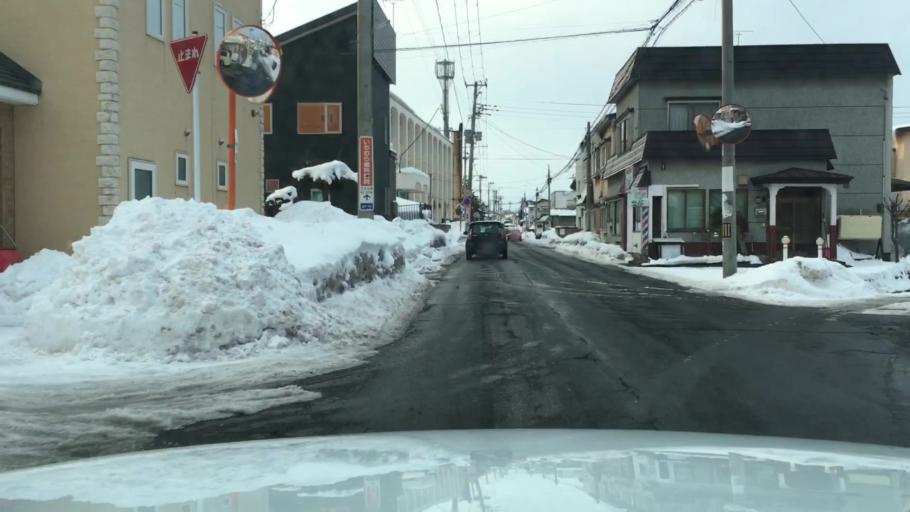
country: JP
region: Aomori
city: Hirosaki
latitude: 40.5827
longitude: 140.4860
